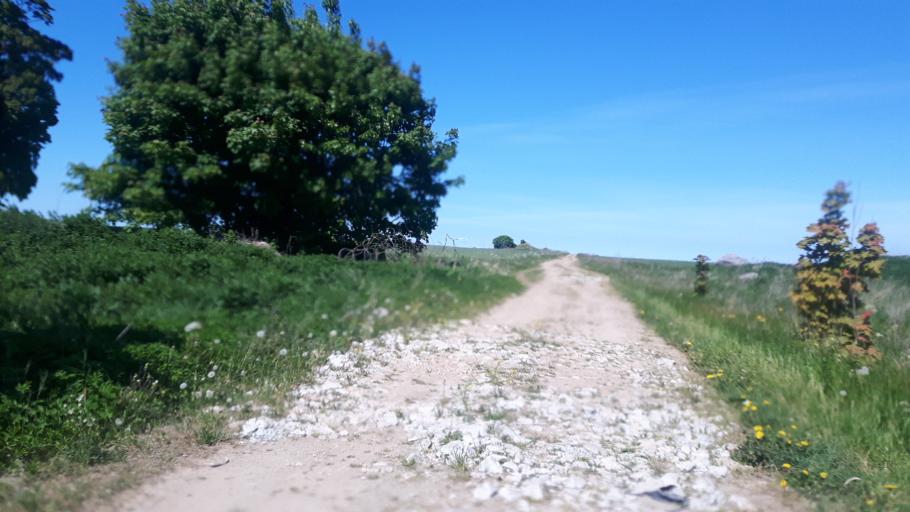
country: EE
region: Ida-Virumaa
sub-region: Toila vald
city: Voka
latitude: 59.4057
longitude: 27.6464
